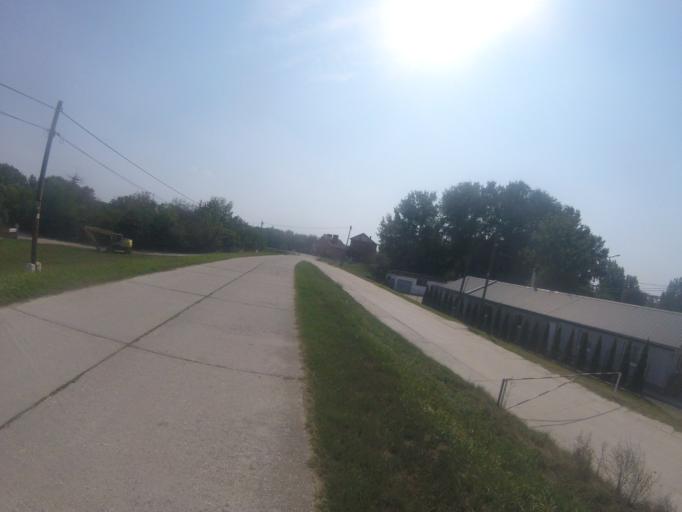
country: HU
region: Bacs-Kiskun
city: Baja
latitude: 46.1951
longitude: 18.9319
